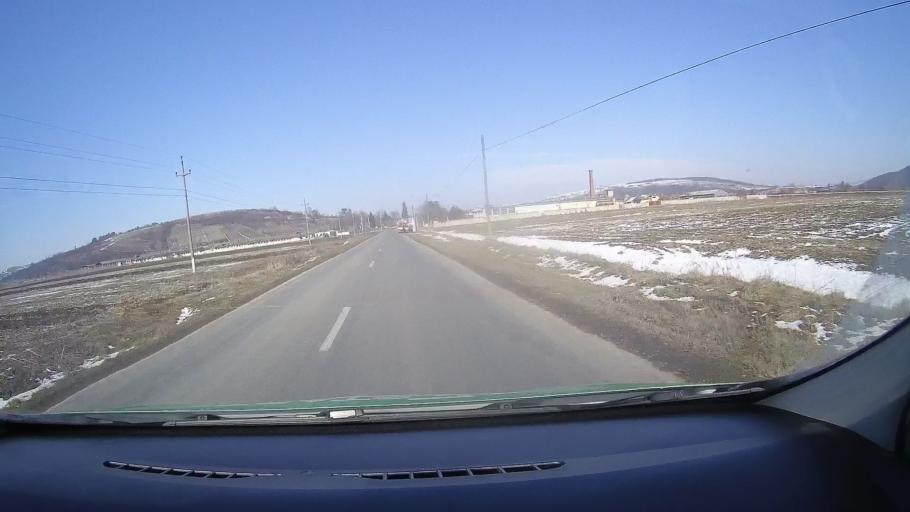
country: RO
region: Brasov
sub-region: Comuna Homorod
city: Homorod
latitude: 46.0325
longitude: 25.2737
